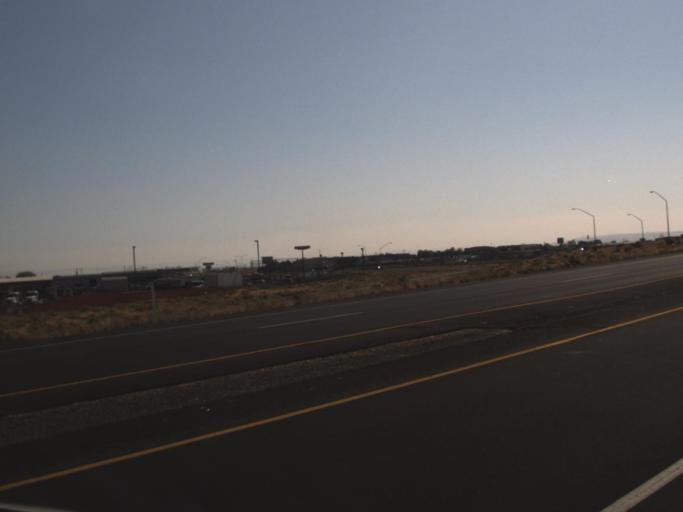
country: US
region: Washington
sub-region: Franklin County
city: Pasco
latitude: 46.2549
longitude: -119.0835
